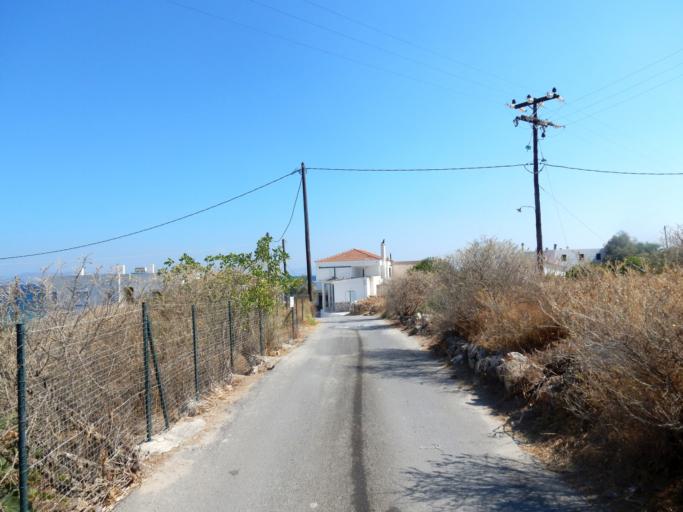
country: GR
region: Attica
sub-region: Nomos Piraios
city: Vathi
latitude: 37.7700
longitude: 23.5373
